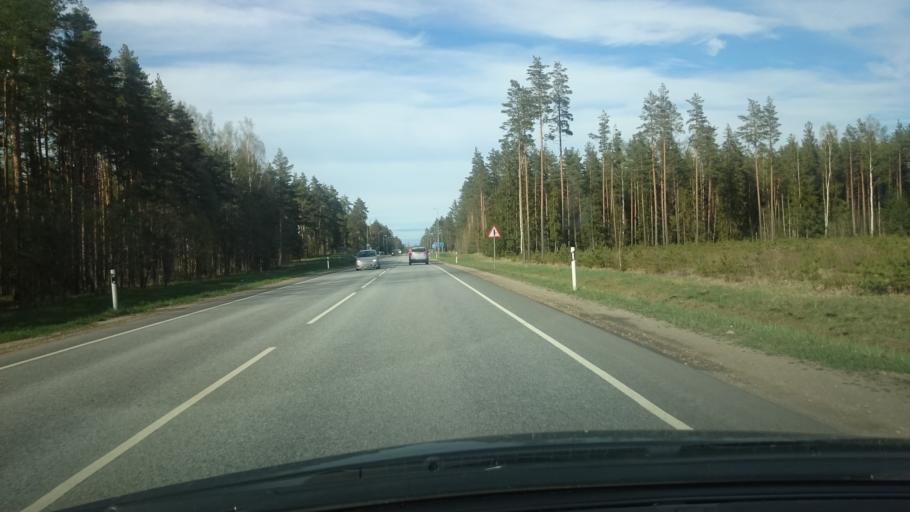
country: EE
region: Ida-Virumaa
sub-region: Toila vald
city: Voka
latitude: 59.3817
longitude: 27.5637
